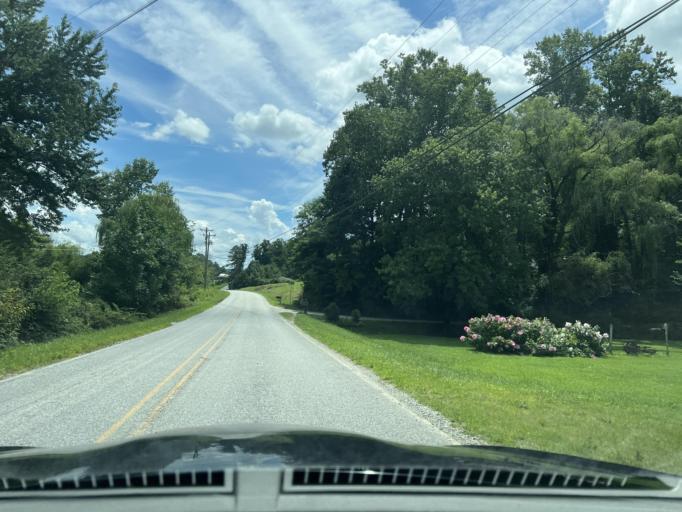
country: US
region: North Carolina
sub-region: Henderson County
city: Fruitland
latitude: 35.4042
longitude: -82.3909
